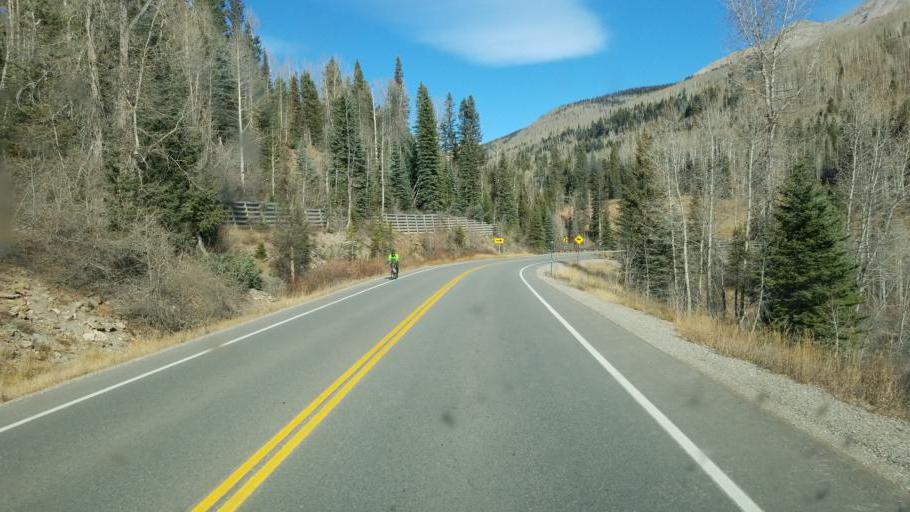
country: US
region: Colorado
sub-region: San Juan County
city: Silverton
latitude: 37.6576
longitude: -107.8112
